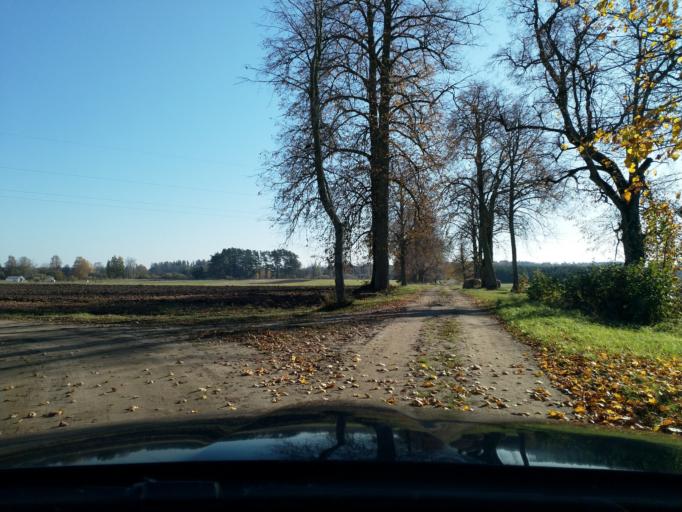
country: LV
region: Skrunda
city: Skrunda
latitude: 56.7769
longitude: 21.9922
